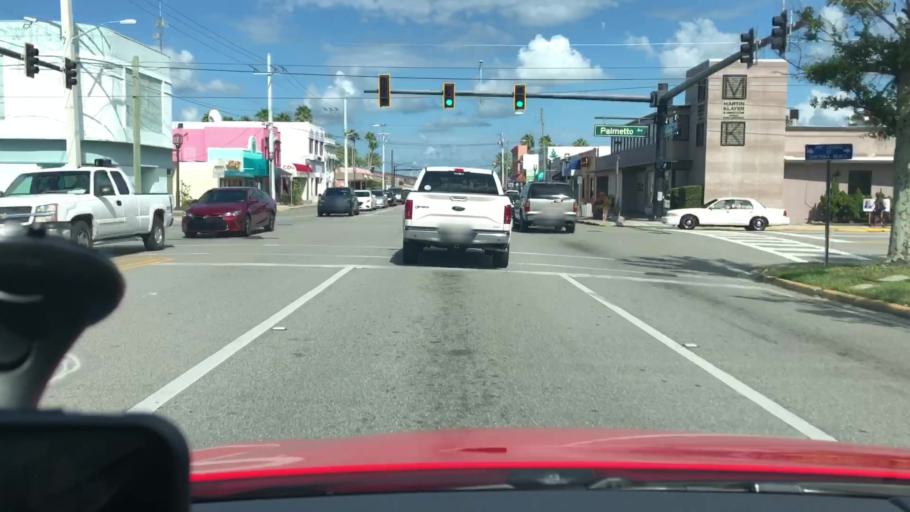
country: US
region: Florida
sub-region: Volusia County
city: Daytona Beach
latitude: 29.2114
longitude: -81.0214
